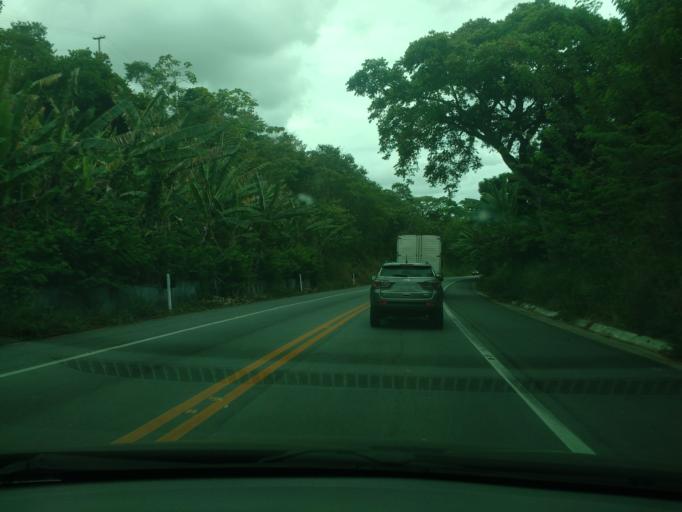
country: BR
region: Alagoas
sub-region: Uniao Dos Palmares
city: Uniao dos Palmares
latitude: -9.2260
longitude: -36.0272
